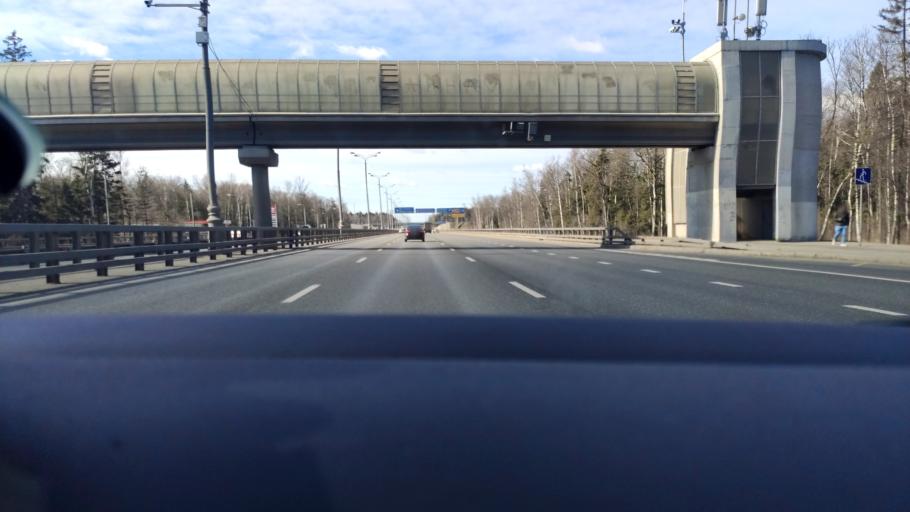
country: RU
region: Moskovskaya
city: Kokoshkino
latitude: 55.5607
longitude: 37.1616
